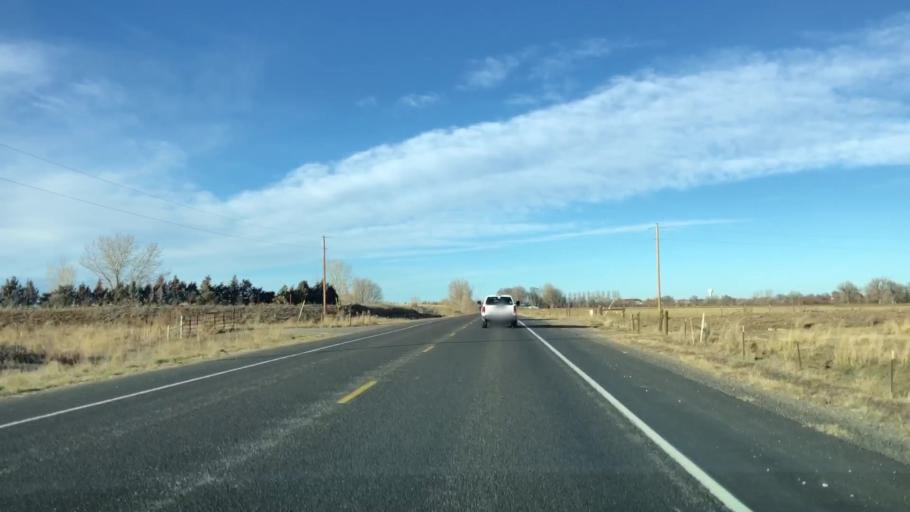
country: US
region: Colorado
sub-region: Weld County
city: Windsor
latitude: 40.5005
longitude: -104.9817
